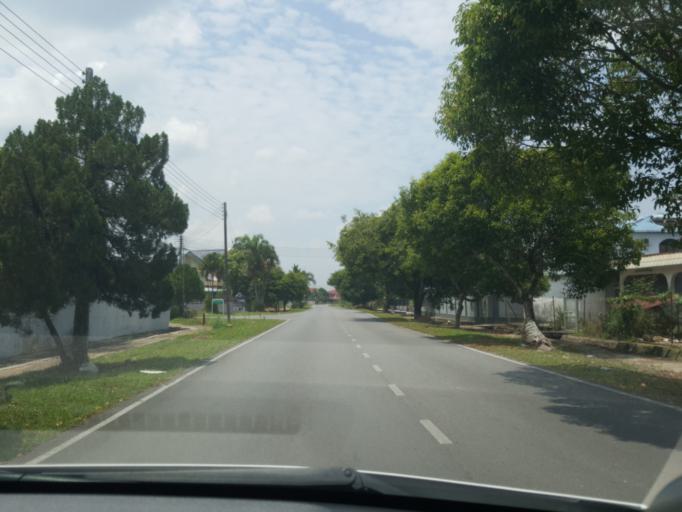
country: MY
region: Sarawak
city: Sarikei
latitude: 2.1227
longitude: 111.5257
